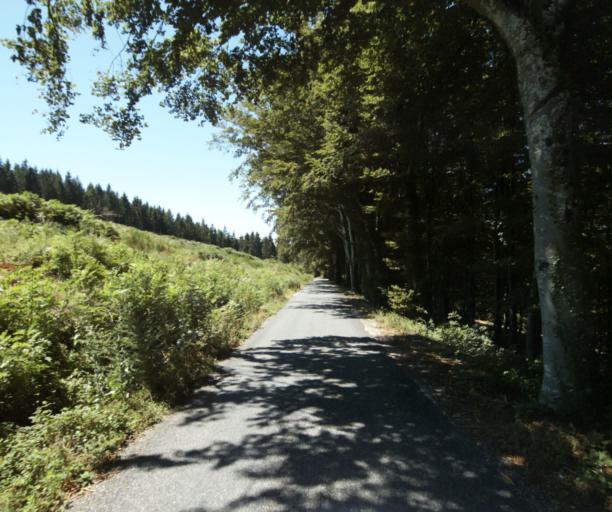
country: FR
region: Midi-Pyrenees
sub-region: Departement du Tarn
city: Dourgne
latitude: 43.4247
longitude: 2.1755
